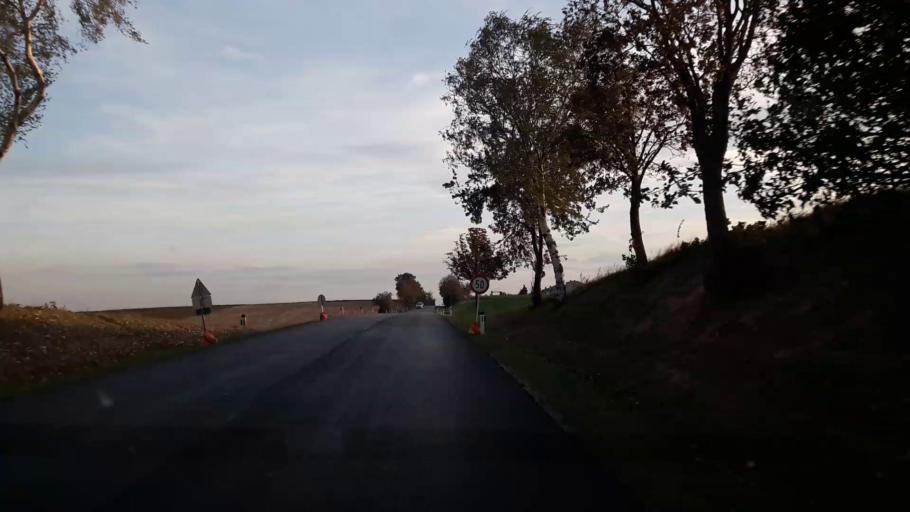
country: AT
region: Lower Austria
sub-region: Politischer Bezirk Korneuburg
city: Grossrussbach
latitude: 48.4692
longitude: 16.3792
